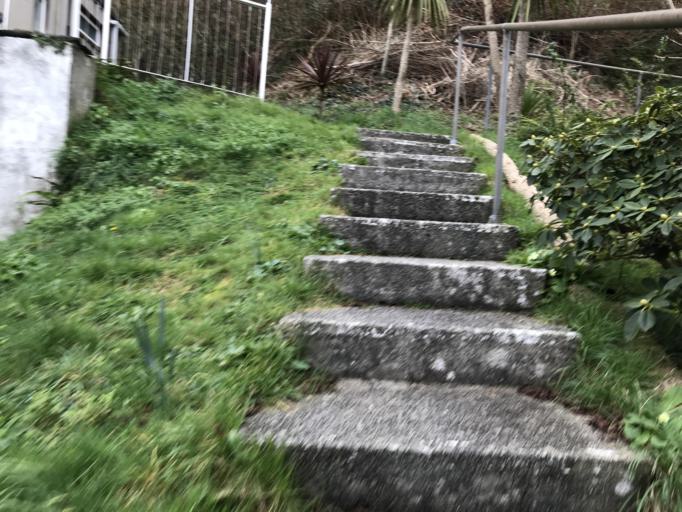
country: GB
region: England
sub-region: Cornwall
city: Looe
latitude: 50.3633
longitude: -4.4369
